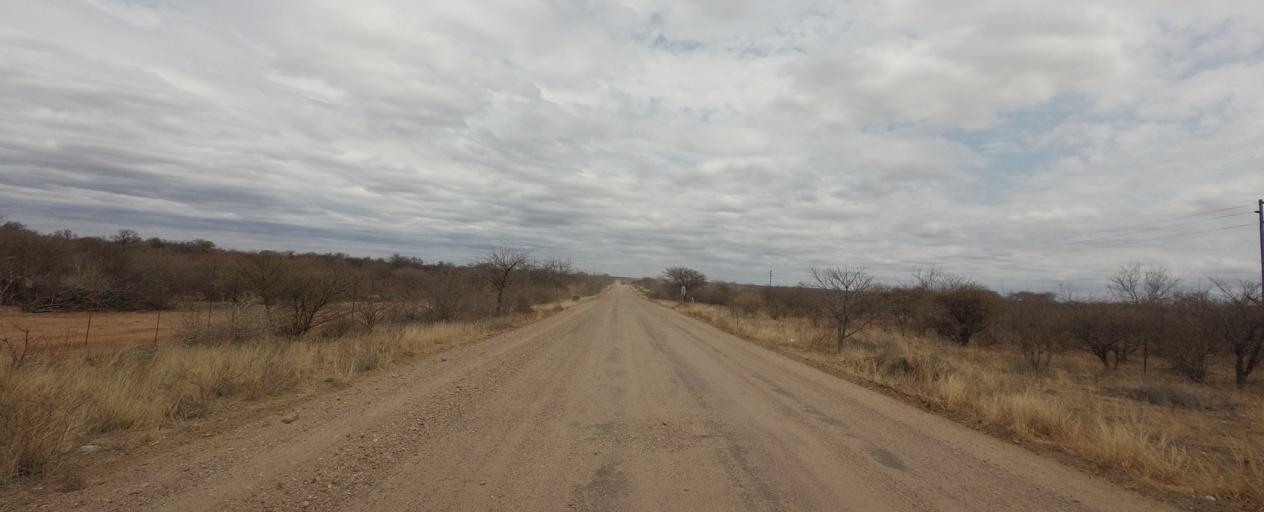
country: BW
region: Central
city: Mathathane
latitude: -22.6789
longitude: 28.6639
